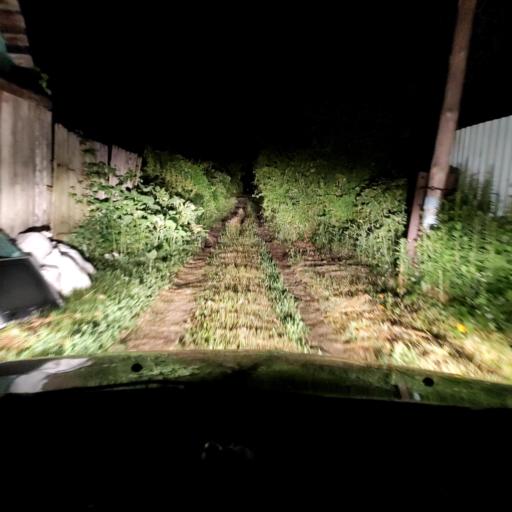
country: RU
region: Voronezj
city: Maslovka
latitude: 51.6071
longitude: 39.2761
